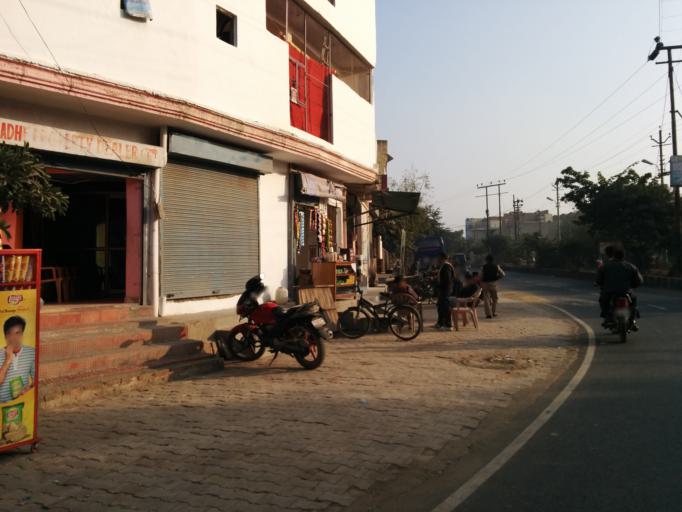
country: IN
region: Uttar Pradesh
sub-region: Mathura
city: Vrindavan
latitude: 27.5671
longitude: 77.6756
